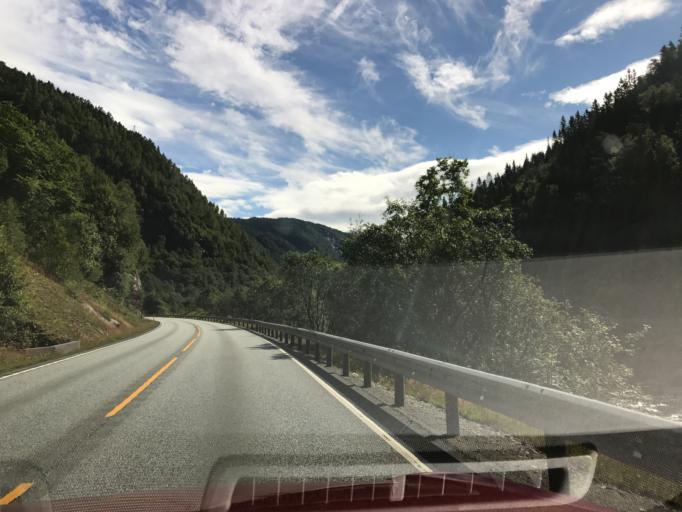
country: NO
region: Hordaland
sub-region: Kvam
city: Oystese
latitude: 60.6467
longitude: 6.1186
